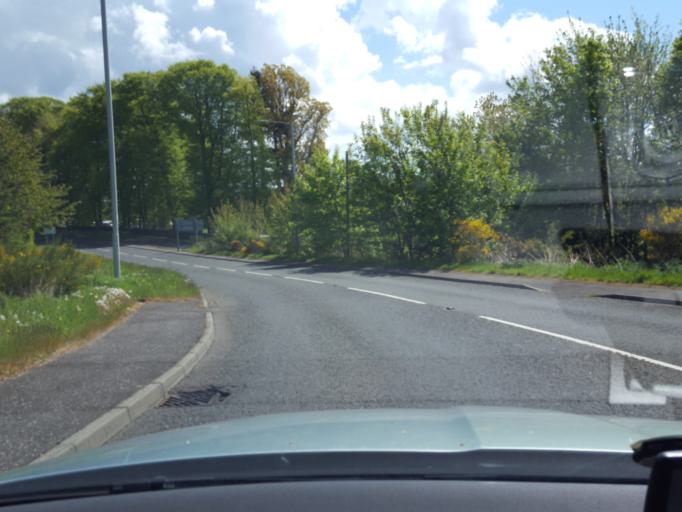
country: GB
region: Scotland
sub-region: Angus
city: Brechin
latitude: 56.7283
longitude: -2.6974
